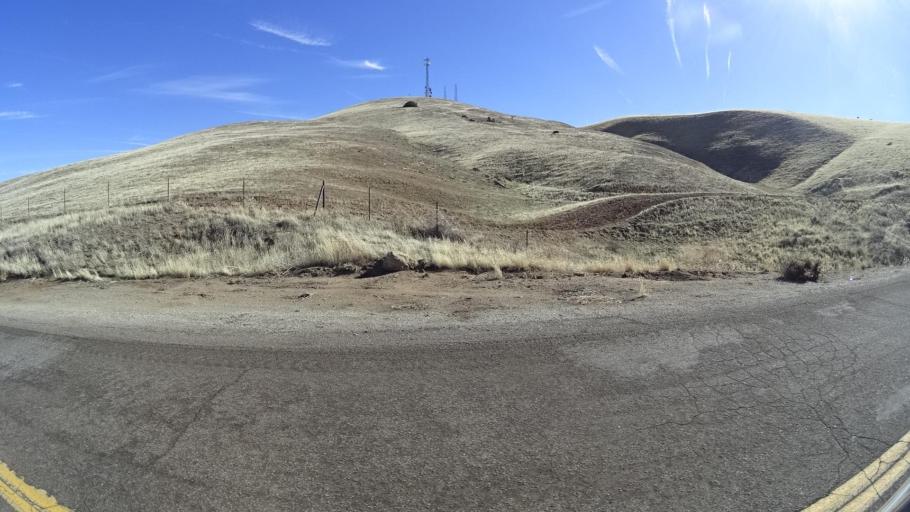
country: US
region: California
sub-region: Kern County
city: Maricopa
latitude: 34.9218
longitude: -119.4101
